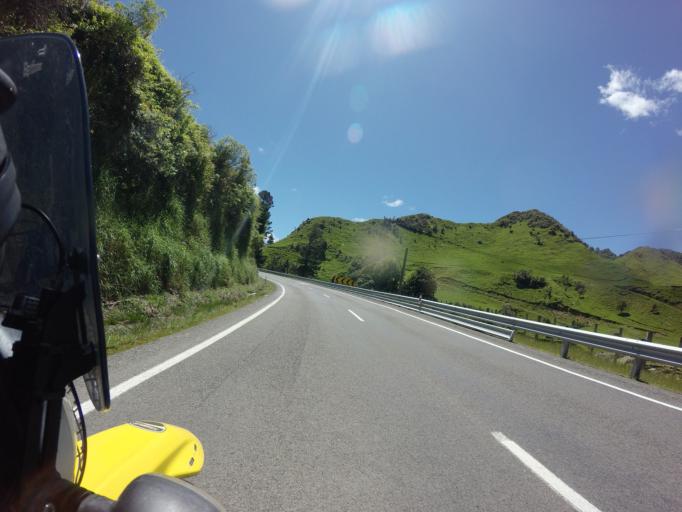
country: NZ
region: Bay of Plenty
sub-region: Opotiki District
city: Opotiki
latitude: -38.3780
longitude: 177.4691
